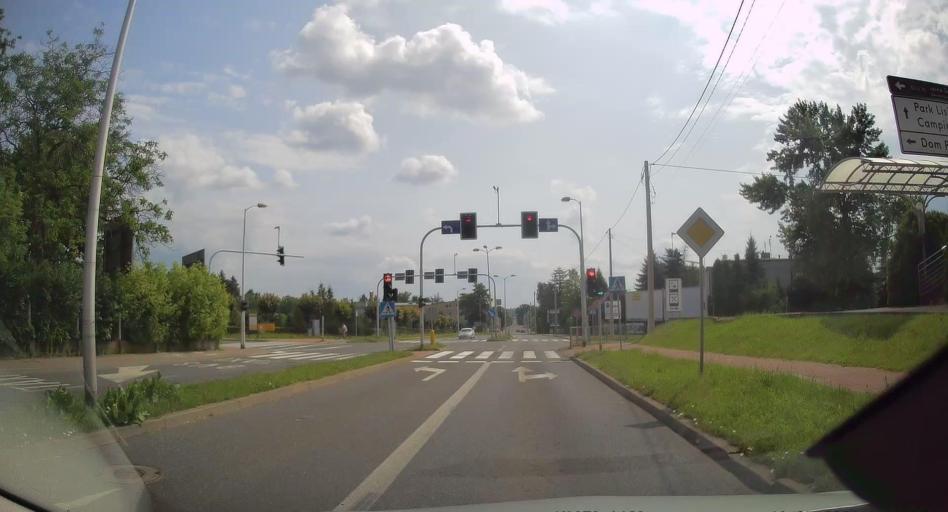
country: PL
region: Silesian Voivodeship
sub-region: Czestochowa
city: Czestochowa
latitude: 50.8146
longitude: 19.0845
